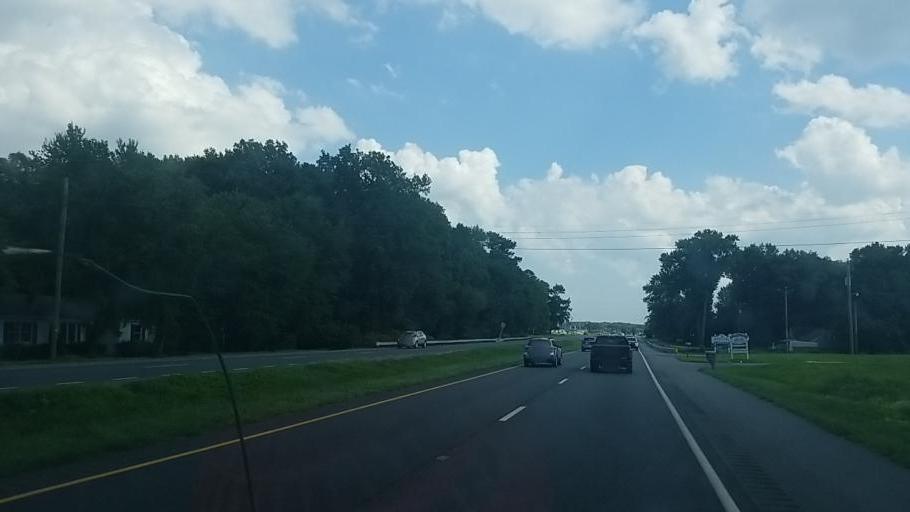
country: US
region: Delaware
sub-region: Sussex County
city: Selbyville
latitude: 38.5279
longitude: -75.2475
